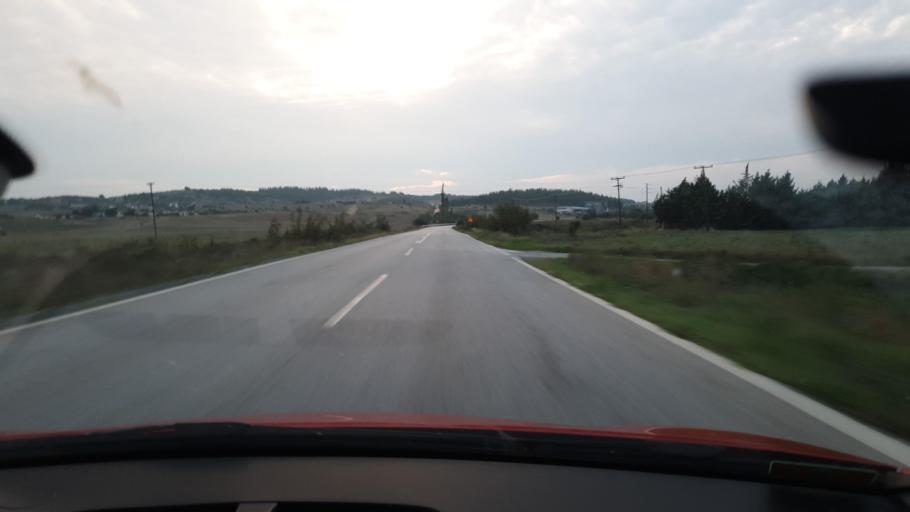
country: GR
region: Central Macedonia
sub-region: Nomos Kilkis
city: Kristoni
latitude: 40.9952
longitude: 22.7458
